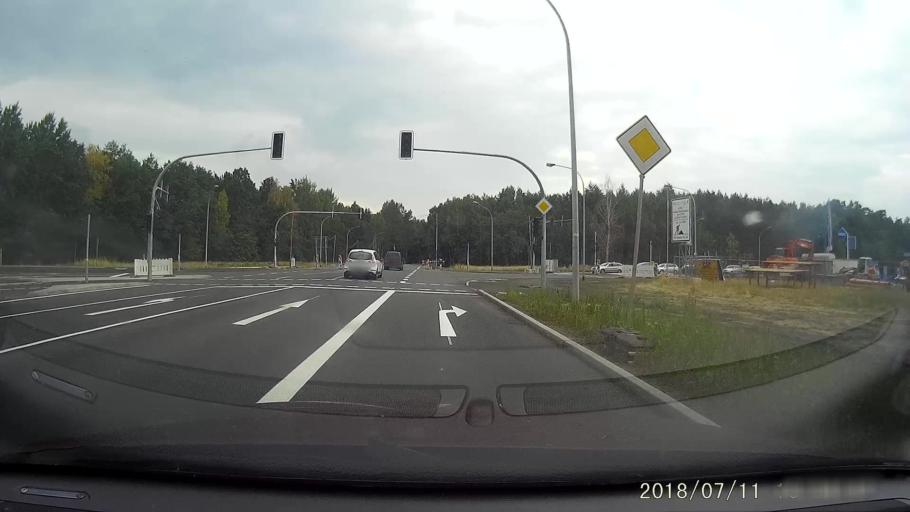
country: DE
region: Saxony
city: Niesky
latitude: 51.2781
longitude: 14.8187
